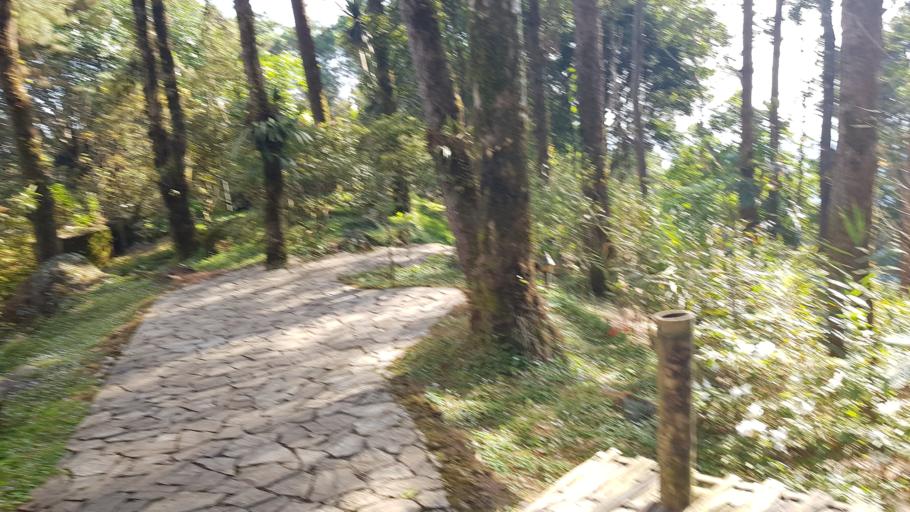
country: TH
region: Chiang Rai
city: Mae Fa Luang
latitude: 20.3355
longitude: 99.8110
